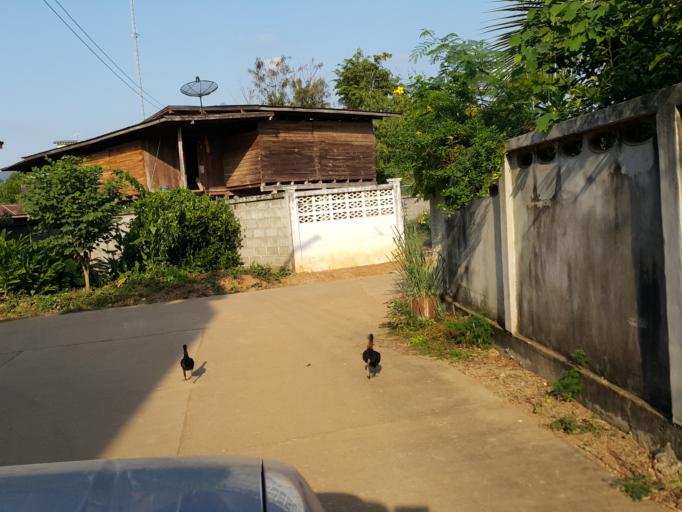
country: TH
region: Sukhothai
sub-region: Amphoe Si Satchanalai
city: Si Satchanalai
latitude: 17.4700
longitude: 99.6488
